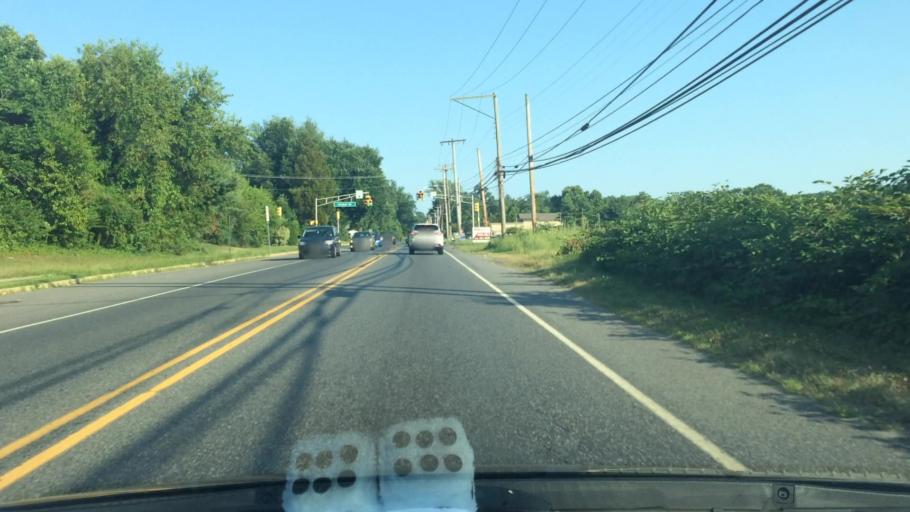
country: US
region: New Jersey
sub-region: Gloucester County
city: Turnersville
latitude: 39.7660
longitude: -75.0417
